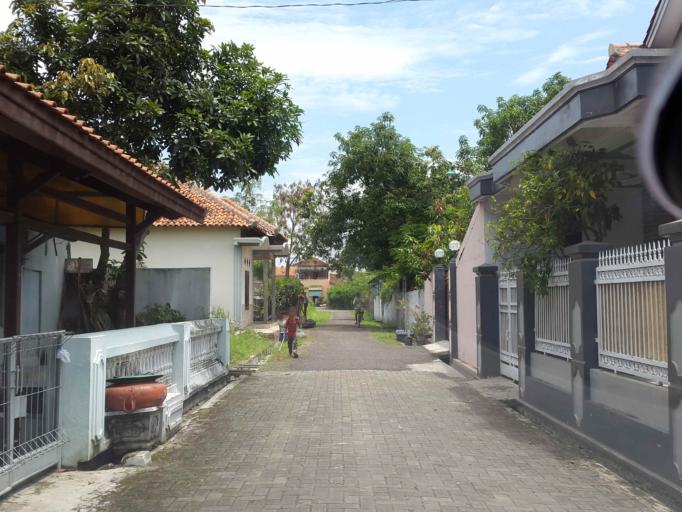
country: ID
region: Central Java
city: Dukuhturi
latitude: -6.8833
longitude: 109.0740
